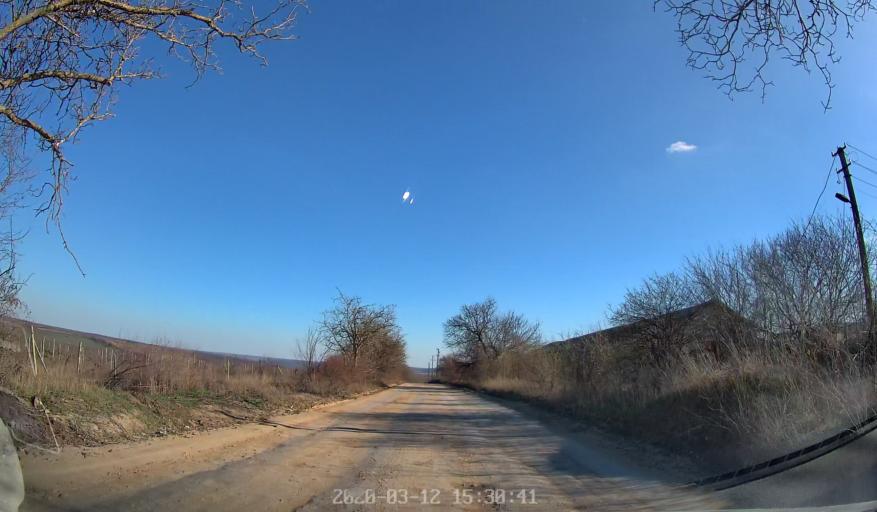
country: MD
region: Chisinau
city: Ciorescu
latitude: 47.1601
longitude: 28.9397
